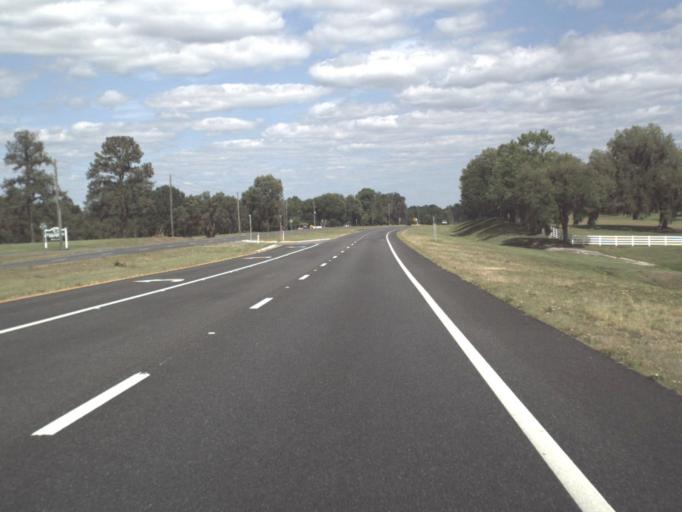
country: US
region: Florida
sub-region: Marion County
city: Ocala
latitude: 29.2310
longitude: -82.2524
